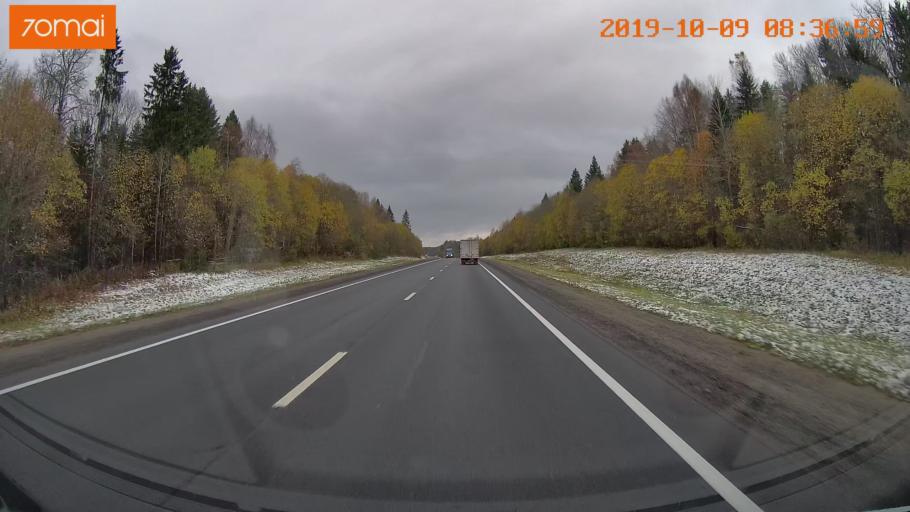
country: RU
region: Vologda
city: Gryazovets
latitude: 58.9345
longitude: 40.1757
